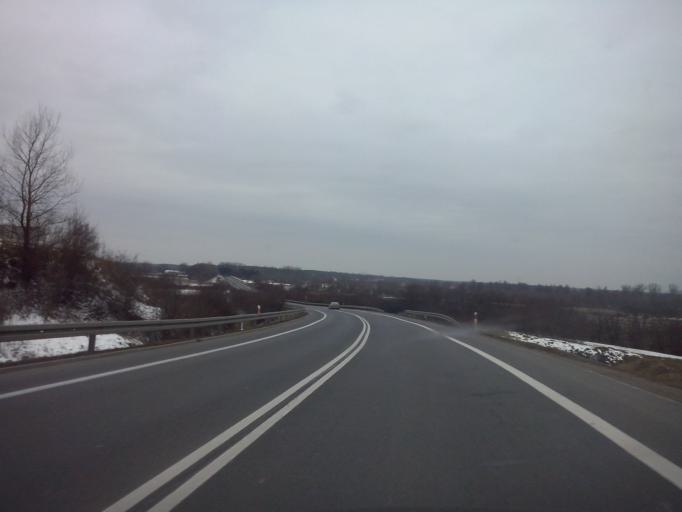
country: PL
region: Subcarpathian Voivodeship
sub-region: Powiat nizanski
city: Zarzecze
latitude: 50.5258
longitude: 22.1918
